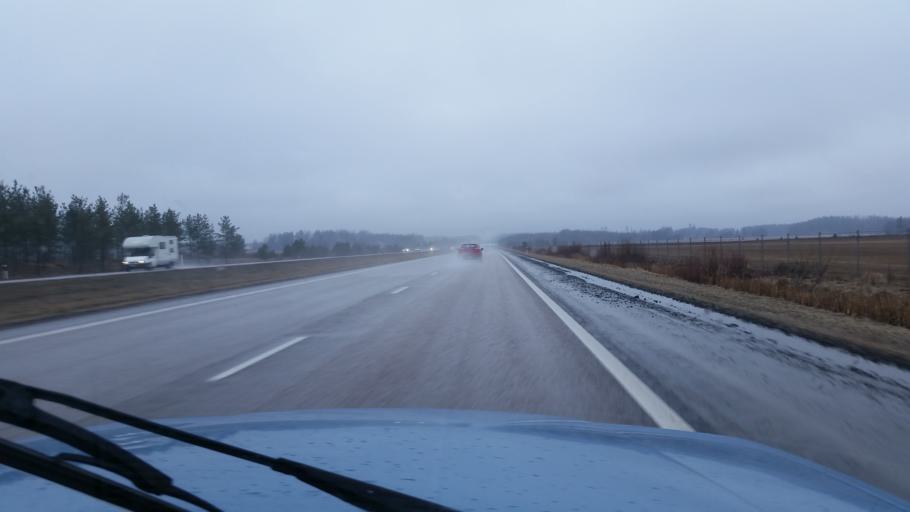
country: FI
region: Uusimaa
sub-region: Helsinki
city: Nurmijaervi
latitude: 60.5206
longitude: 24.8457
